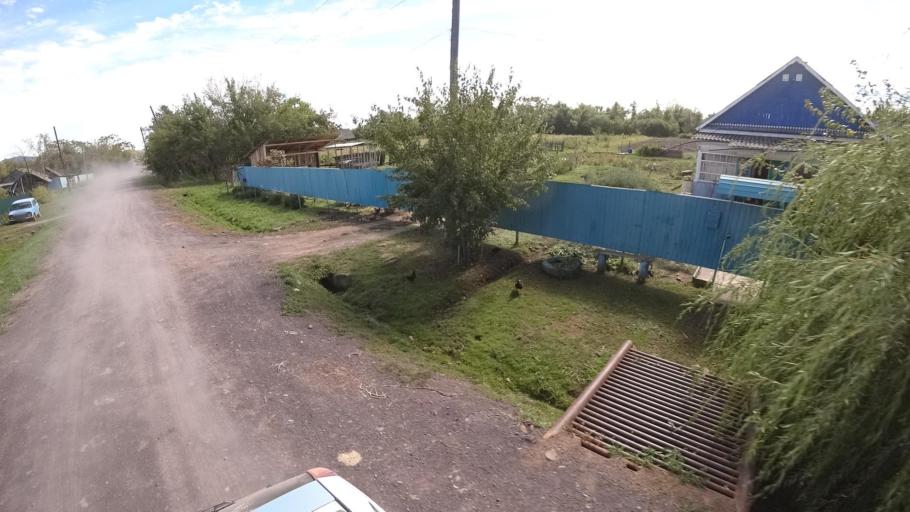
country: RU
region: Primorskiy
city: Yakovlevka
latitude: 44.4362
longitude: 133.5633
